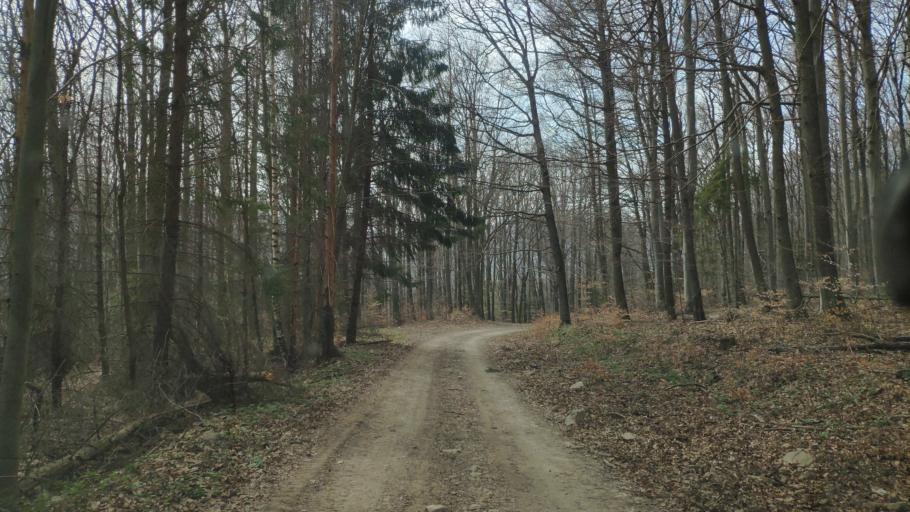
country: SK
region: Kosicky
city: Moldava nad Bodvou
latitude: 48.7425
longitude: 21.0390
